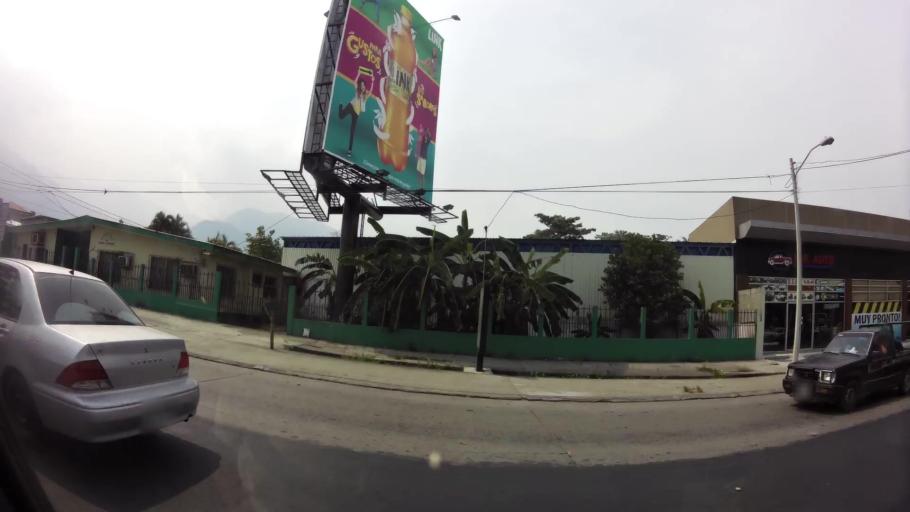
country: HN
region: Cortes
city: San Pedro Sula
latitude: 15.5188
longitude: -88.0290
